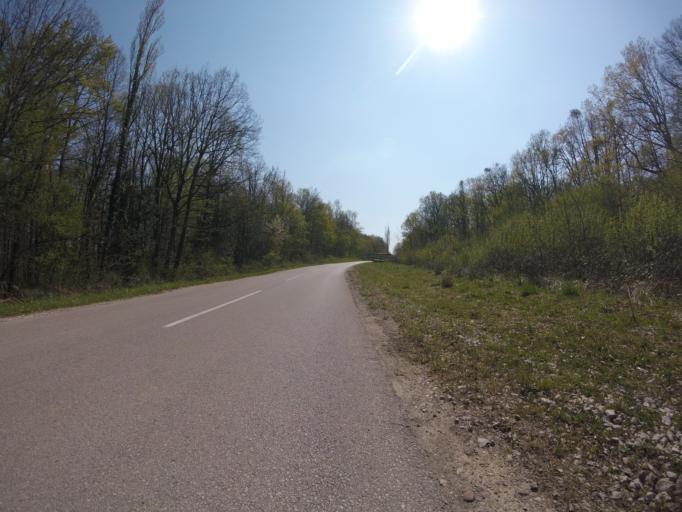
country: HR
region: Zagrebacka
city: Lukavec
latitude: 45.6318
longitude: 15.9625
